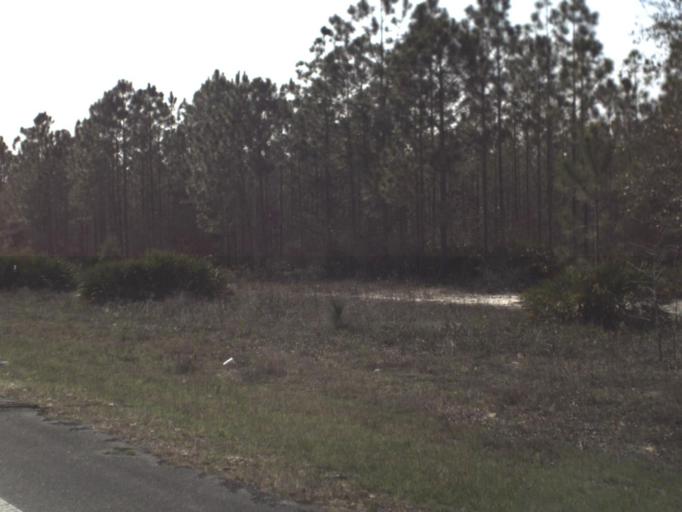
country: US
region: Florida
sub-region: Franklin County
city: Carrabelle
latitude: 29.9356
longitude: -84.5059
